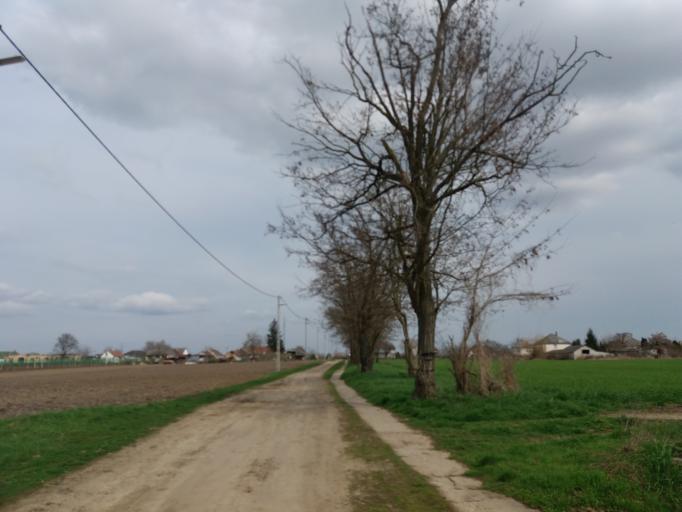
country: HU
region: Szabolcs-Szatmar-Bereg
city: Petnehaza
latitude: 48.0560
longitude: 22.0399
